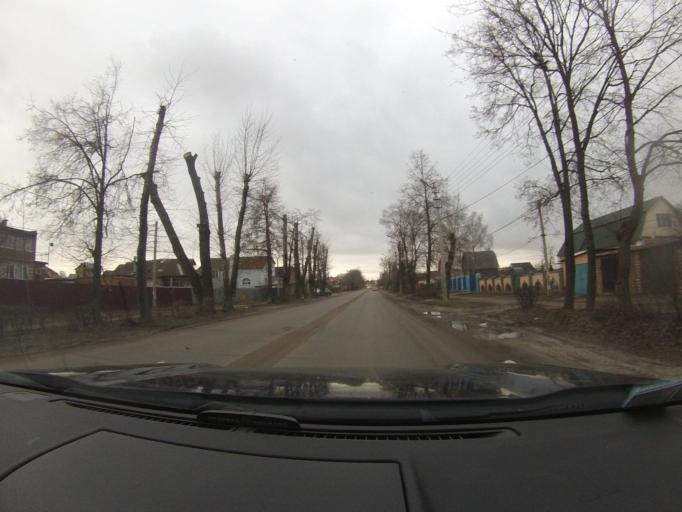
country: RU
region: Moskovskaya
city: Lopatinskiy
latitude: 55.3257
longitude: 38.6962
